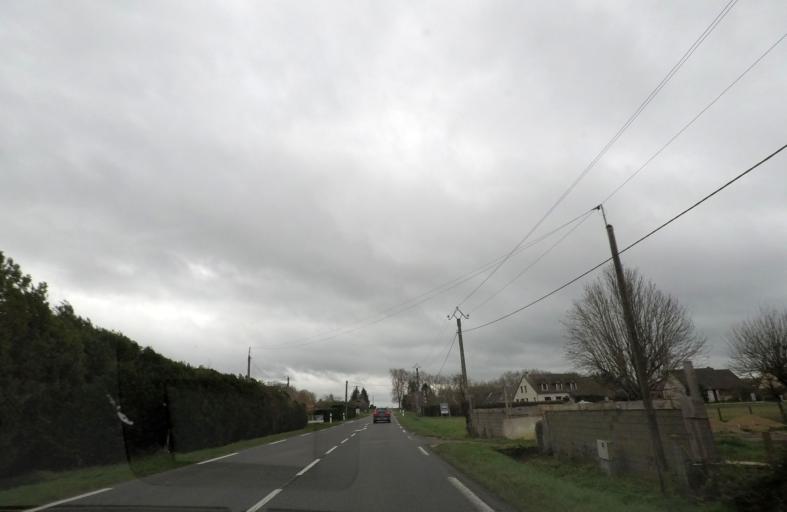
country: FR
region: Centre
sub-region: Departement du Loir-et-Cher
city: Cour-Cheverny
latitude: 47.5251
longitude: 1.4325
